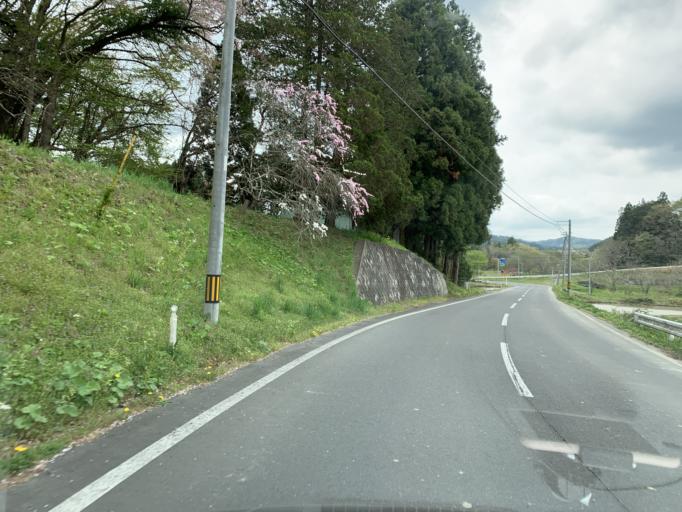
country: JP
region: Iwate
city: Ichinoseki
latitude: 38.8376
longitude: 141.3550
